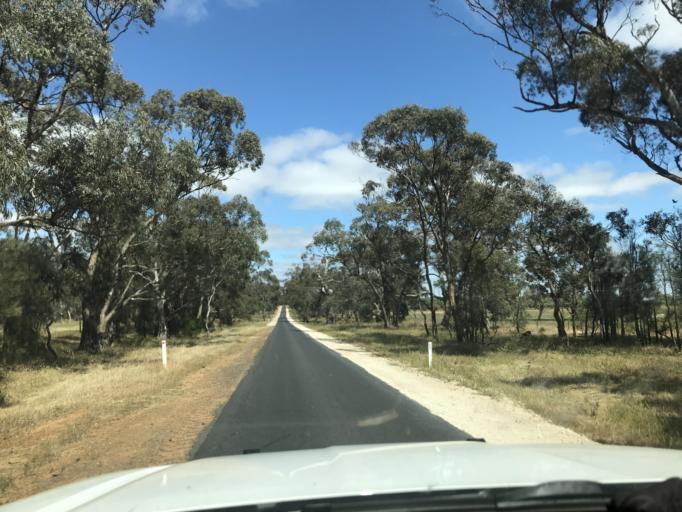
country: AU
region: South Australia
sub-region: Tatiara
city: Bordertown
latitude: -36.3063
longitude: 141.0696
